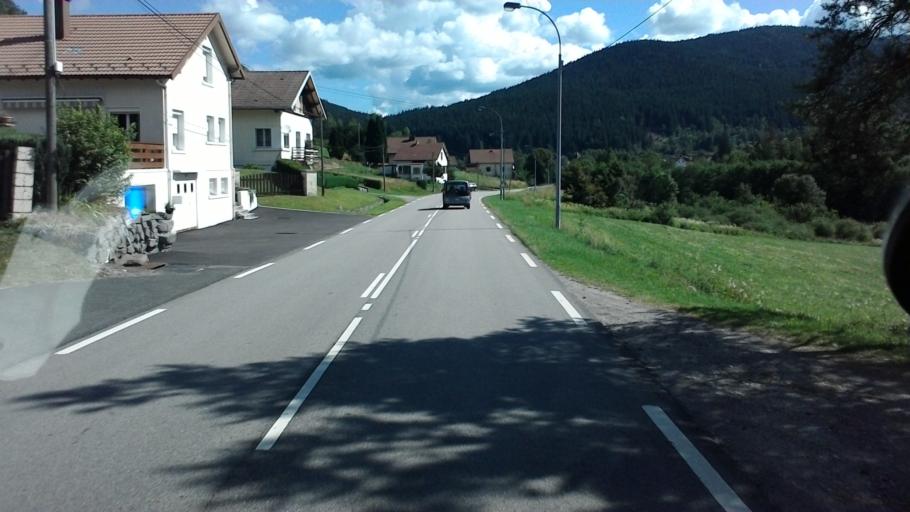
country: FR
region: Lorraine
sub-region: Departement des Vosges
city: Cornimont
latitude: 47.9398
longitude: 6.8283
